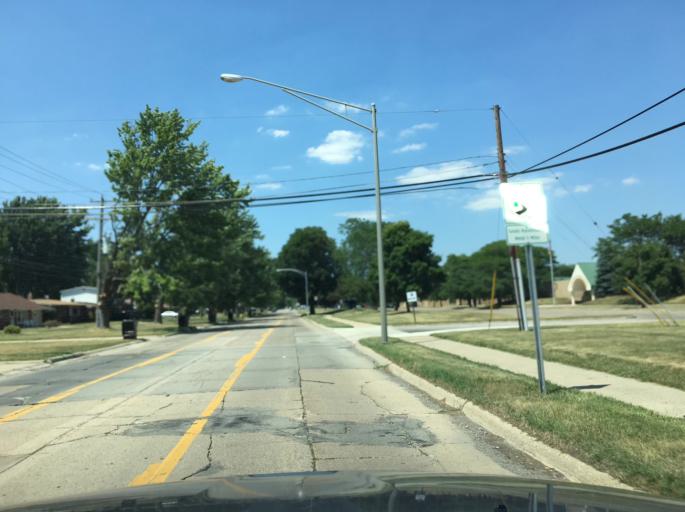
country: US
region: Michigan
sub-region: Macomb County
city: Clinton
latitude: 42.5557
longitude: -82.9103
